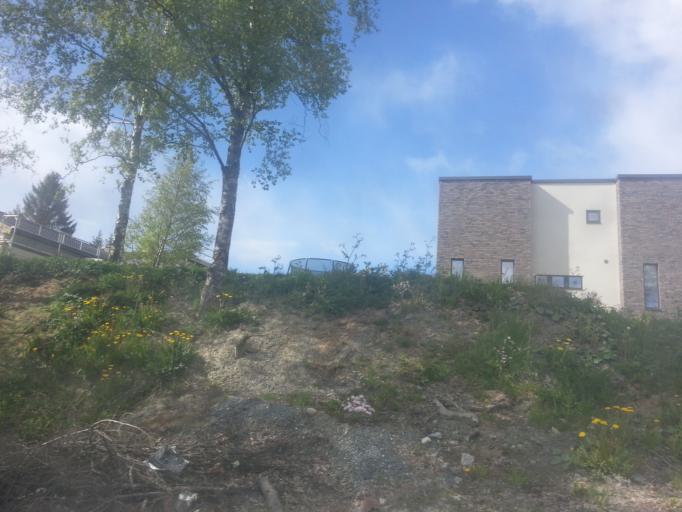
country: NO
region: Sor-Trondelag
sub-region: Trondheim
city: Trondheim
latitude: 63.4157
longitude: 10.4242
